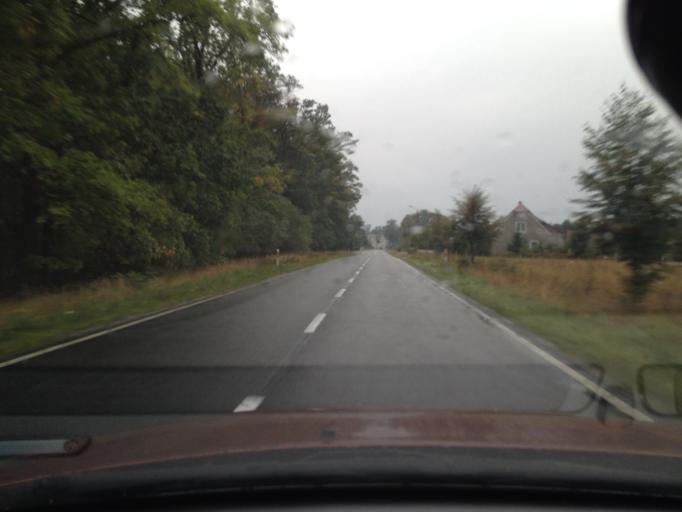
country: PL
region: Lubusz
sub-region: Powiat zaganski
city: Ilowa
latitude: 51.5351
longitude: 15.2418
